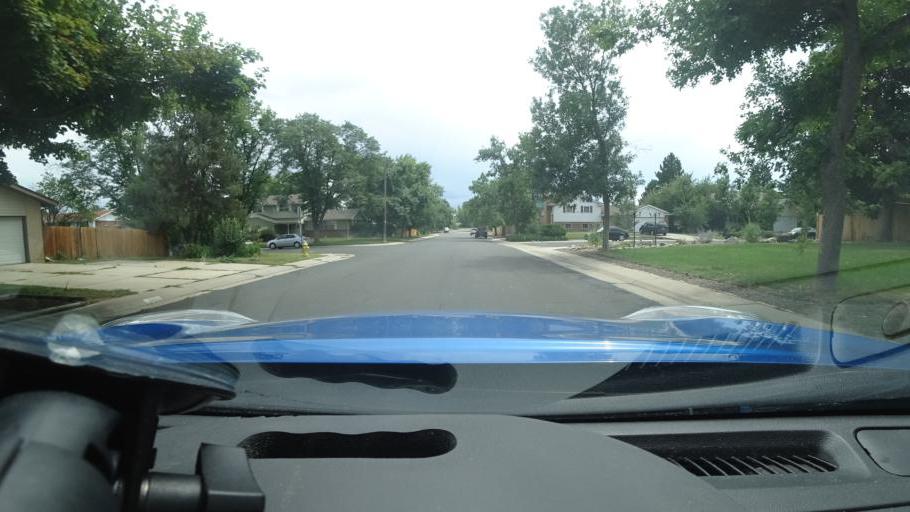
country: US
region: Colorado
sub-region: Adams County
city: Aurora
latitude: 39.7208
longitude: -104.8332
